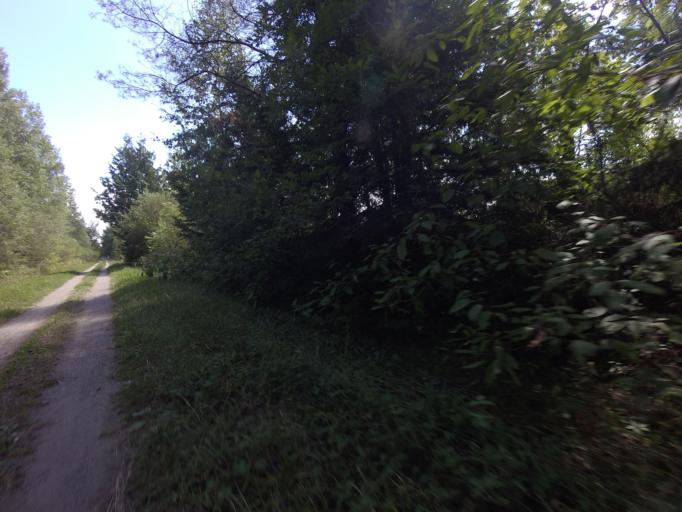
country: CA
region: Ontario
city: Orangeville
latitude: 43.7752
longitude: -80.1978
